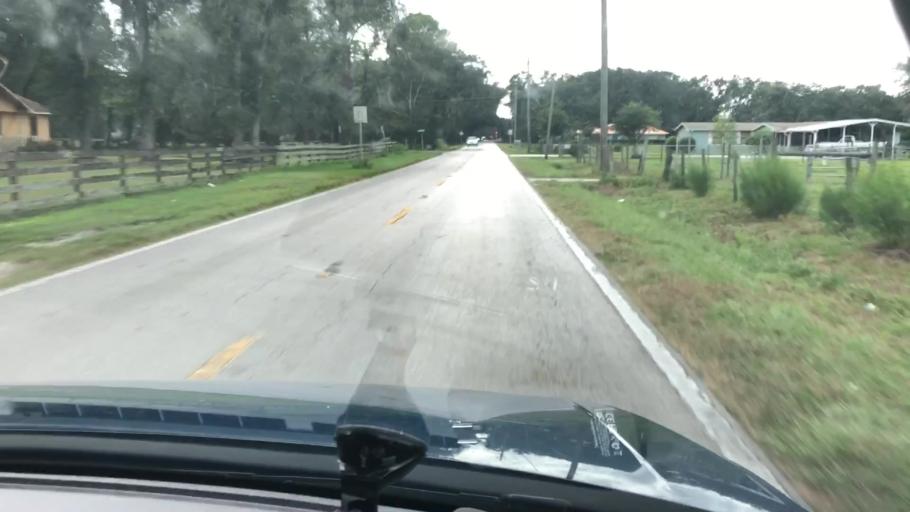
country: US
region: Florida
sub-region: Polk County
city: Kathleen
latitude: 28.1243
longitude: -82.0346
